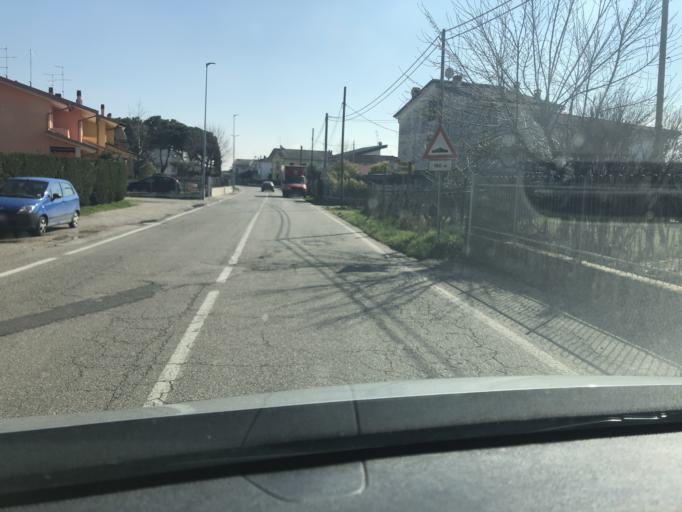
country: IT
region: Veneto
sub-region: Provincia di Verona
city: Villafranca di Verona
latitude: 45.3624
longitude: 10.8383
